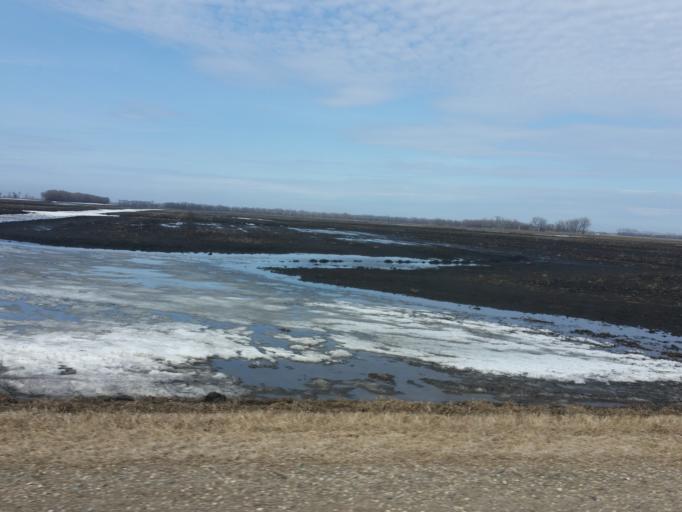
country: US
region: North Dakota
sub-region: Walsh County
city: Grafton
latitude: 48.4265
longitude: -97.2211
